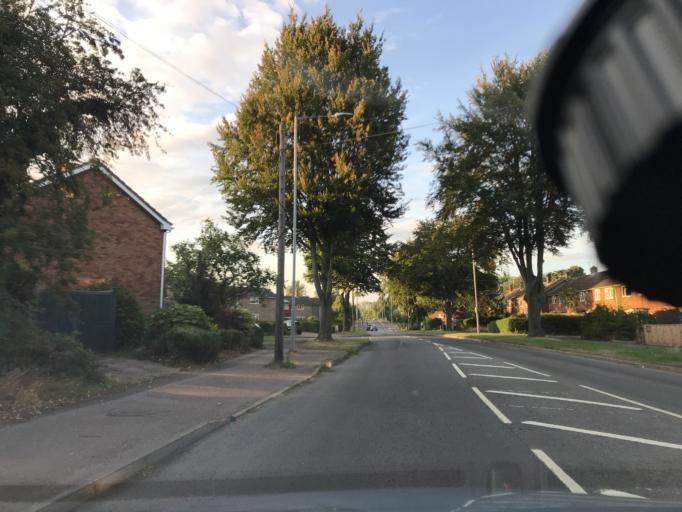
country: GB
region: England
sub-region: Buckinghamshire
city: Aylesbury
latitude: 51.8162
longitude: -0.7904
